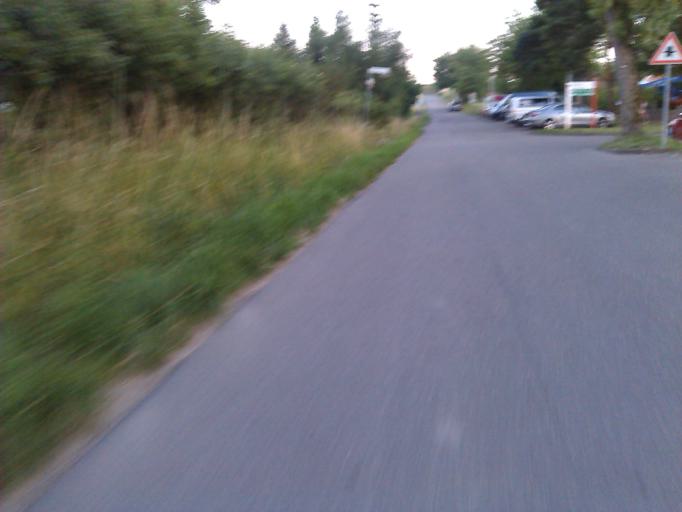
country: DE
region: Baden-Wuerttemberg
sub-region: Regierungsbezirk Stuttgart
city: Leingarten
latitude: 49.1346
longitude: 9.1173
